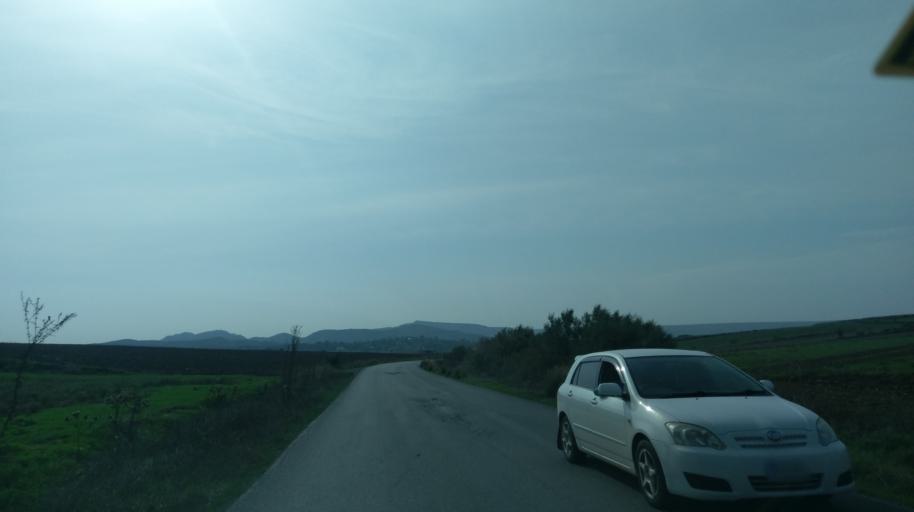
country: CY
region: Keryneia
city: Lapithos
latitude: 35.2853
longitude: 33.1233
